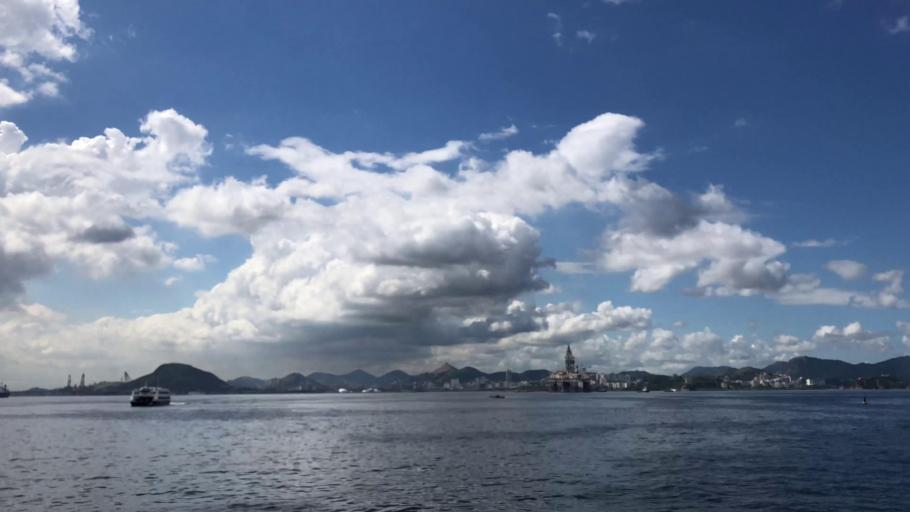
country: BR
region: Rio de Janeiro
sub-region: Rio De Janeiro
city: Rio de Janeiro
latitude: -22.8994
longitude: -43.1595
